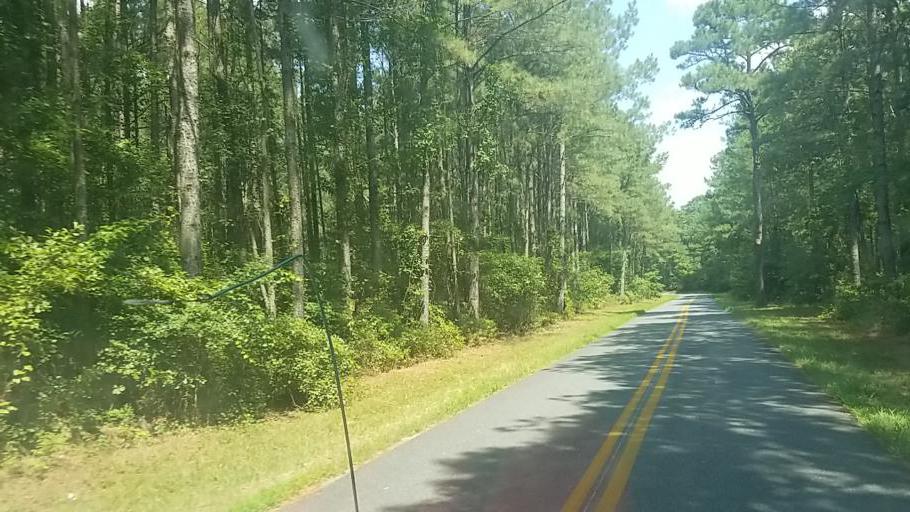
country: US
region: Maryland
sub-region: Worcester County
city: Snow Hill
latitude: 38.2791
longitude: -75.4748
